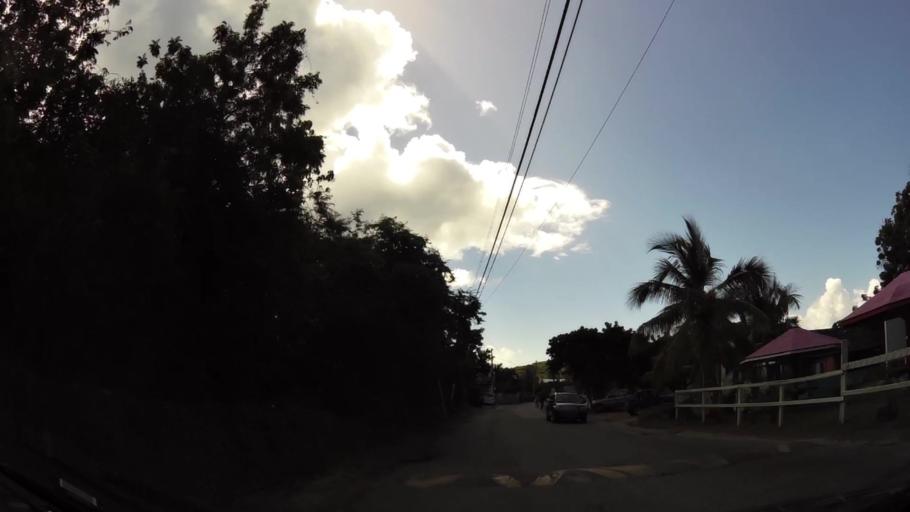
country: VG
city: Tortola
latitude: 18.4460
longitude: -64.4375
